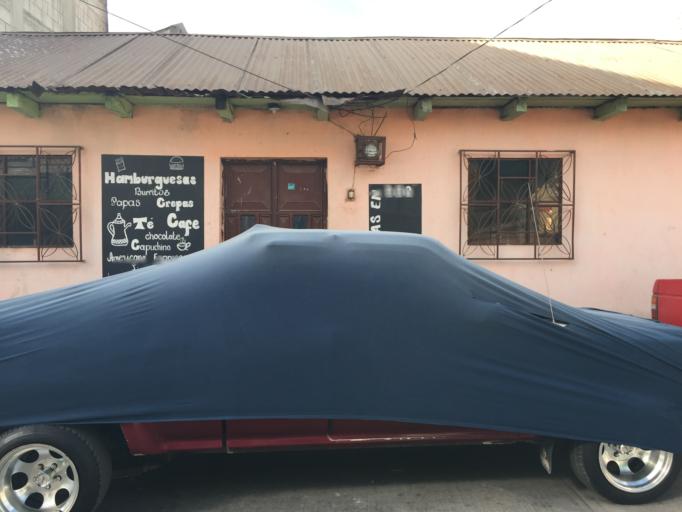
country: GT
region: Quetzaltenango
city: Ostuncalco
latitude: 14.8663
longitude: -91.6238
